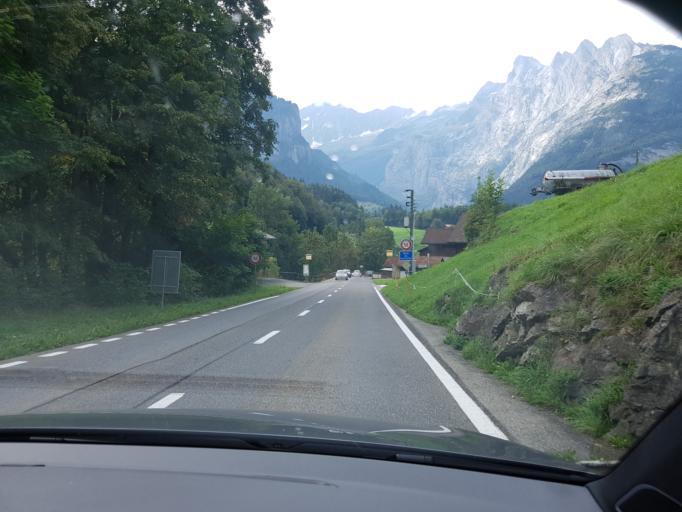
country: CH
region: Bern
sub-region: Interlaken-Oberhasli District
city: Meiringen
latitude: 46.7108
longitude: 8.2475
